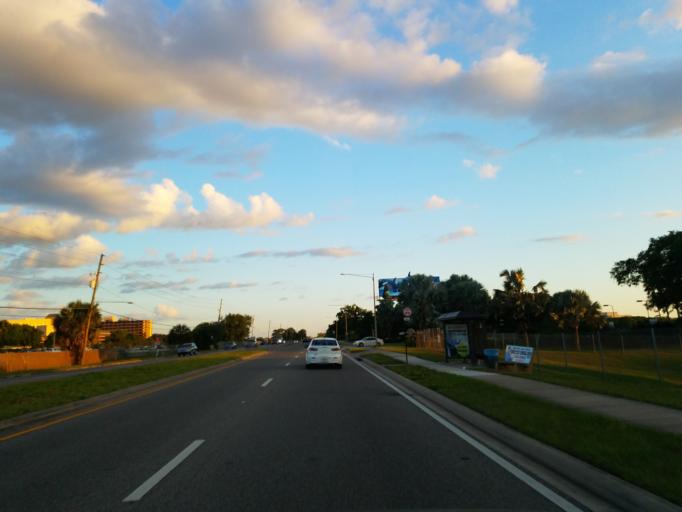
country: US
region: Florida
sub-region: Orange County
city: Doctor Phillips
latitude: 28.4364
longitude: -81.4751
